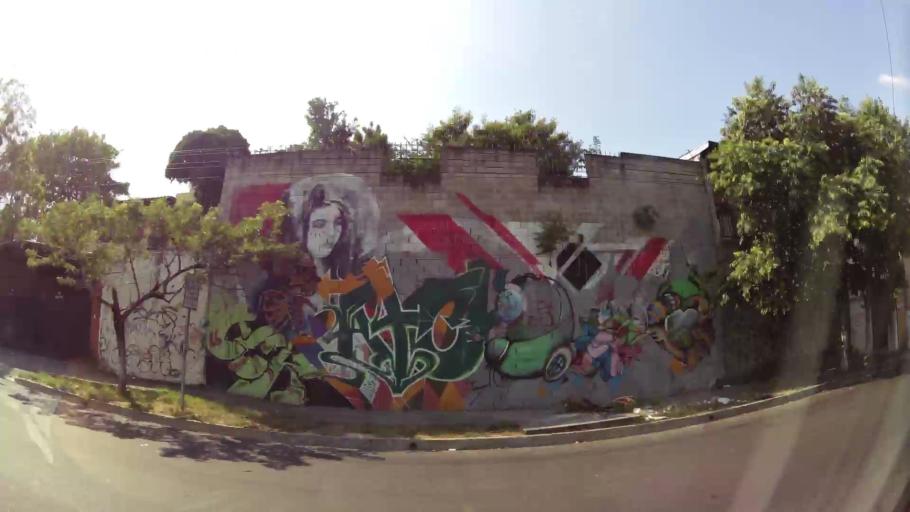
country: SV
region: San Salvador
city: Mejicanos
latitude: 13.7199
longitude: -89.2167
